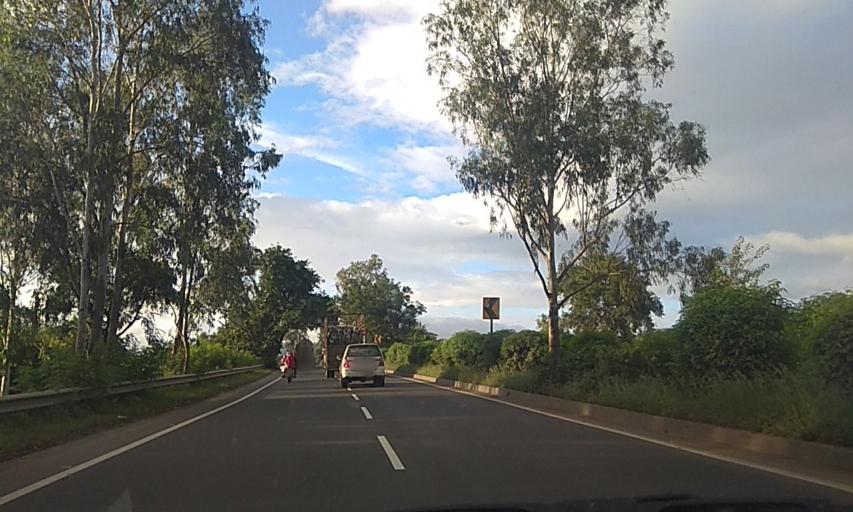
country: IN
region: Maharashtra
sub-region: Satara Division
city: Satara
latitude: 17.5773
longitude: 74.0501
